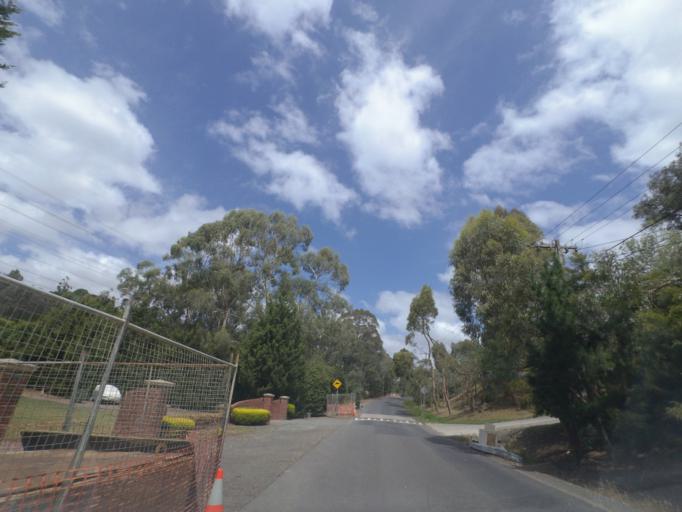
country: AU
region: Victoria
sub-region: Manningham
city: Park Orchards
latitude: -37.7968
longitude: 145.2109
